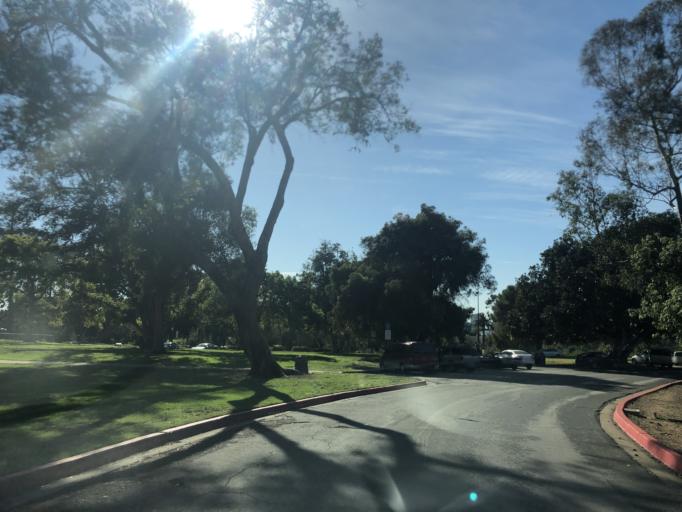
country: US
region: California
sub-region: San Diego County
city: San Diego
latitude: 32.7209
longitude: -117.1405
